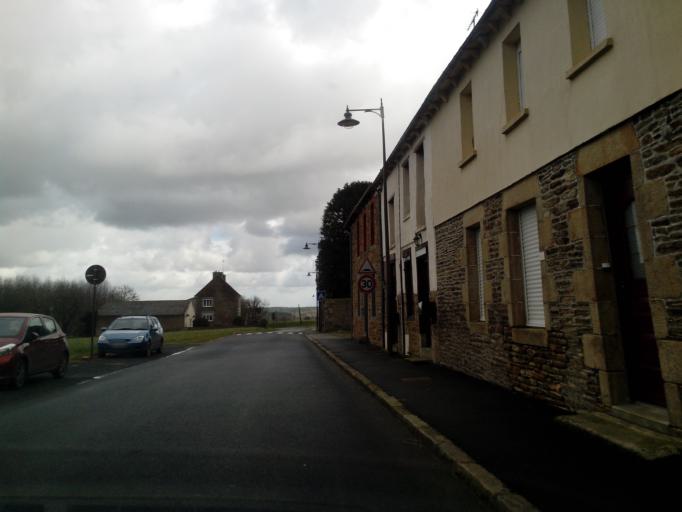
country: FR
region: Brittany
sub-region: Departement des Cotes-d'Armor
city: Sevignac
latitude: 48.2745
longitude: -2.3449
